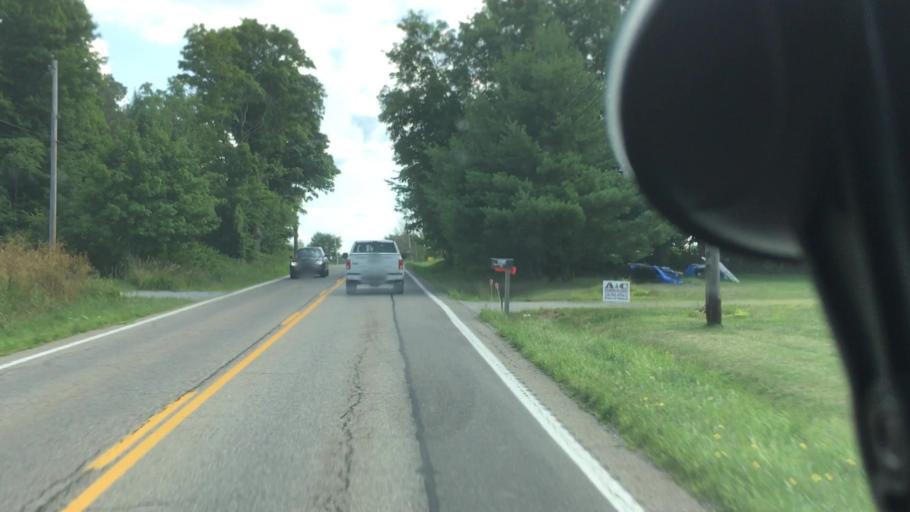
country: US
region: Ohio
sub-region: Columbiana County
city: Salem
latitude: 40.9698
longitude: -80.8288
